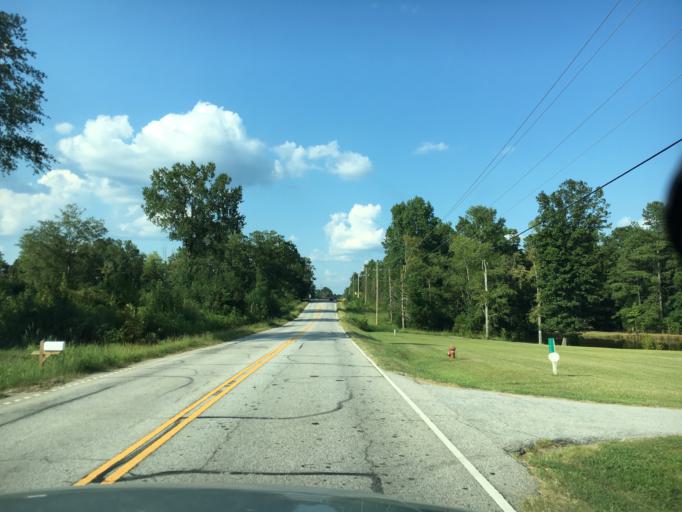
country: US
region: South Carolina
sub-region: Laurens County
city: Clinton
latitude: 34.4902
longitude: -81.8692
